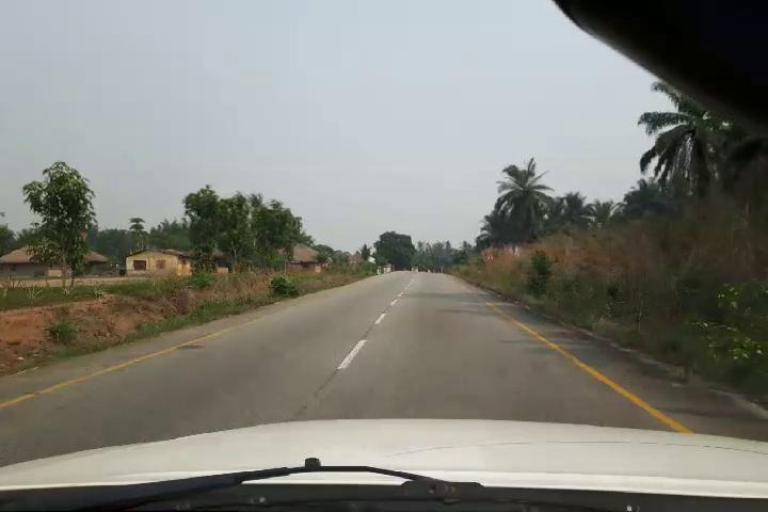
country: SL
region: Southern Province
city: Largo
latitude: 8.2211
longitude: -12.0753
